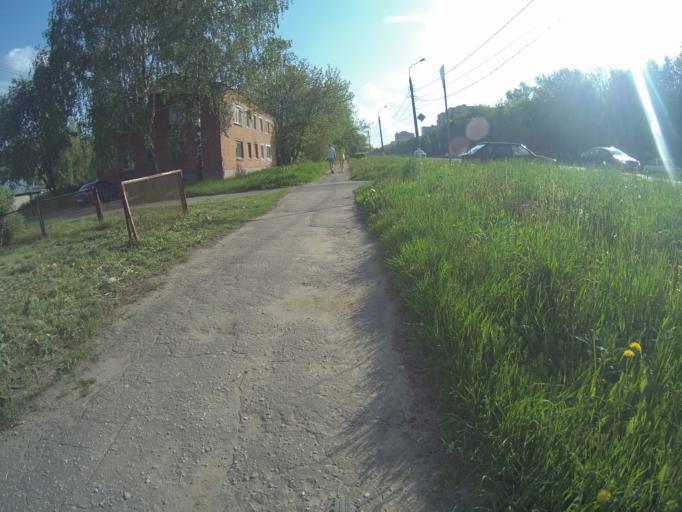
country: RU
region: Vladimir
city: Bogolyubovo
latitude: 56.1702
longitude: 40.4892
